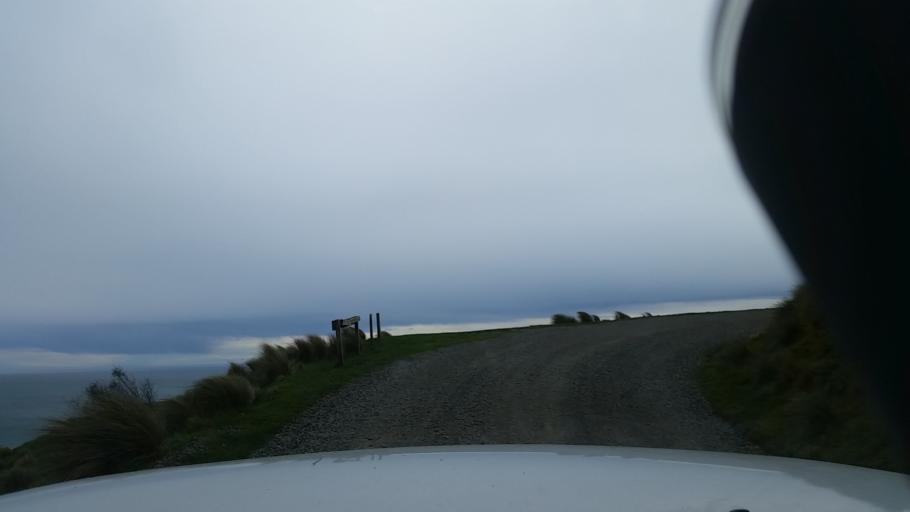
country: NZ
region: Canterbury
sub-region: Christchurch City
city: Christchurch
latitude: -43.8557
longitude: 172.7647
